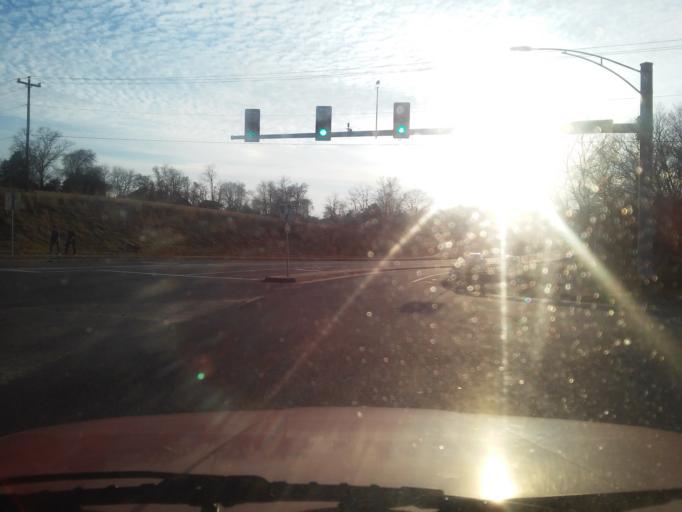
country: US
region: Virginia
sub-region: City of Charlottesville
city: Charlottesville
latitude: 38.0615
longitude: -78.4628
